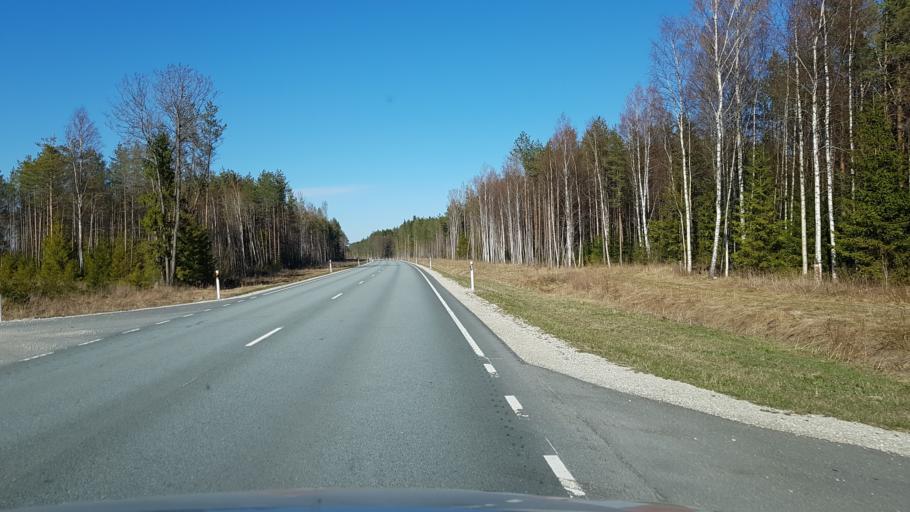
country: EE
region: Jogevamaa
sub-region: Mustvee linn
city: Mustvee
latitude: 58.8655
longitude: 26.9354
